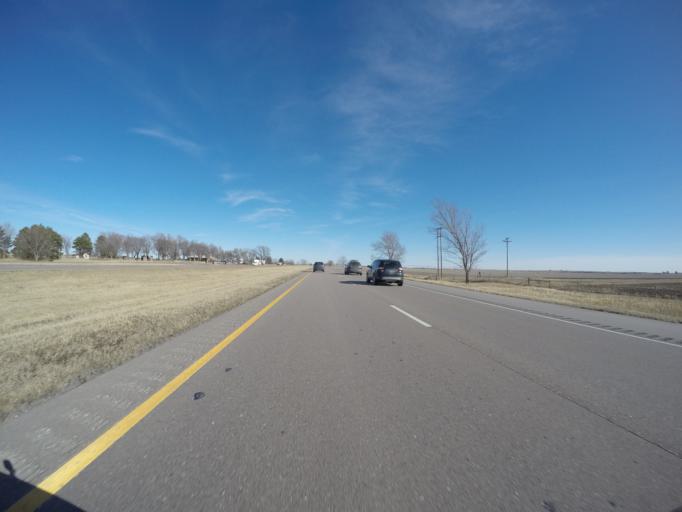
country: US
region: Nebraska
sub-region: York County
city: York
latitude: 40.8219
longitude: -97.5596
